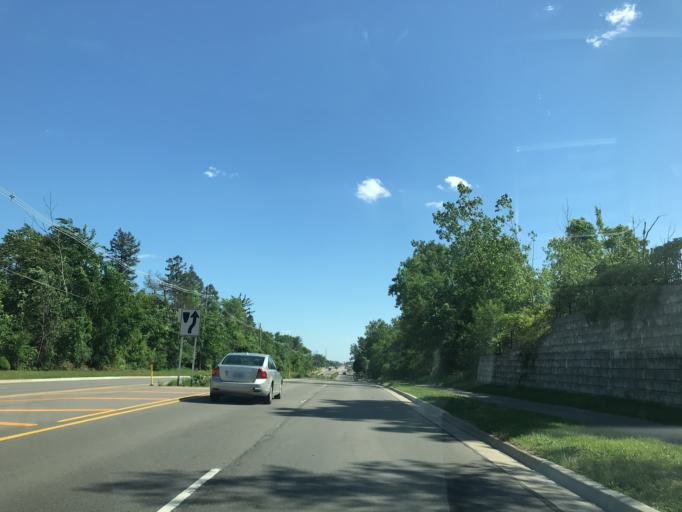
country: US
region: Michigan
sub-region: Oakland County
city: Novi
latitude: 42.4999
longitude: -83.4766
